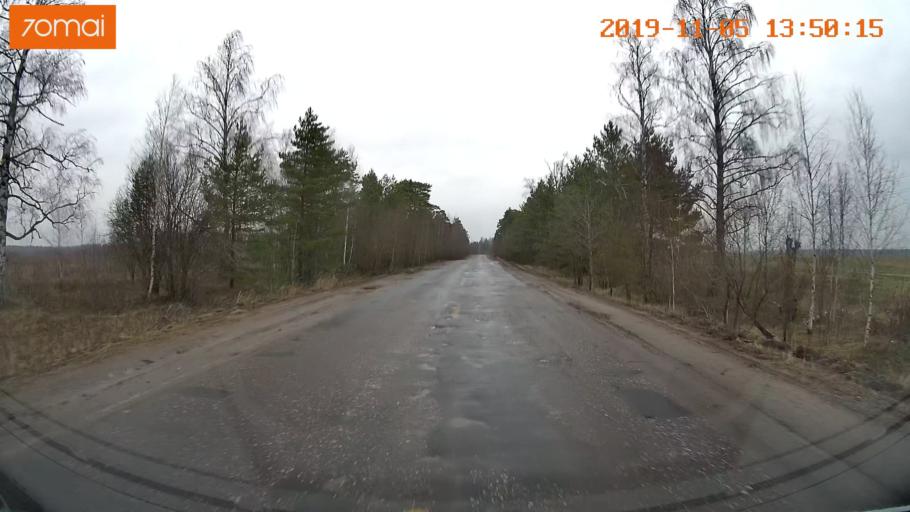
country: RU
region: Ivanovo
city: Kaminskiy
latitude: 57.0180
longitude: 41.4088
